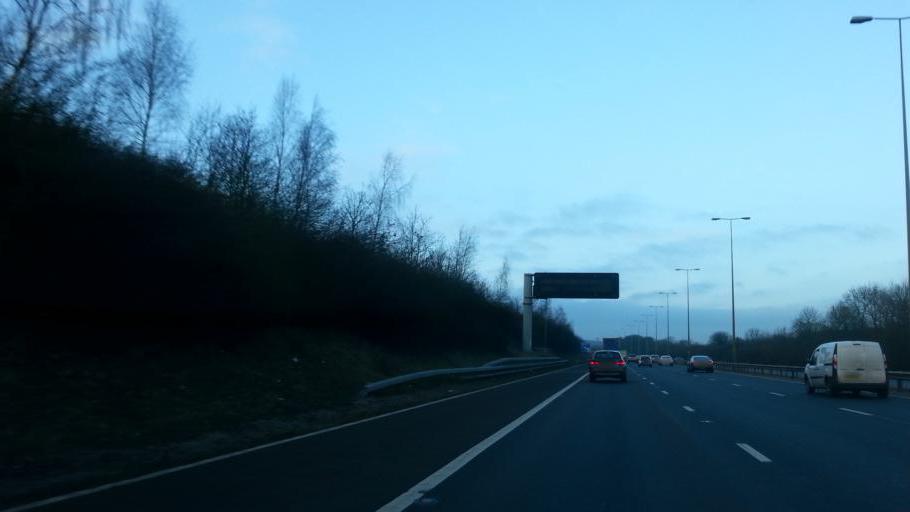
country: GB
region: England
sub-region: Worcestershire
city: Kempsey
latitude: 52.1460
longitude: -2.1937
